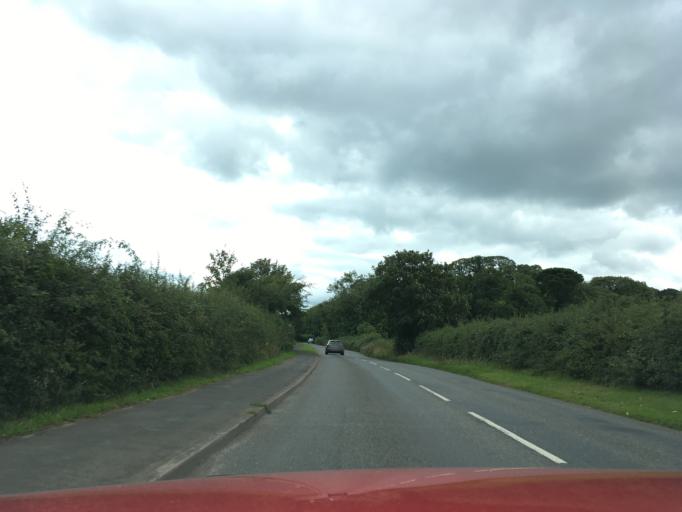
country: GB
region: England
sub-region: Devon
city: Dawlish
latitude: 50.5918
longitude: -3.4544
